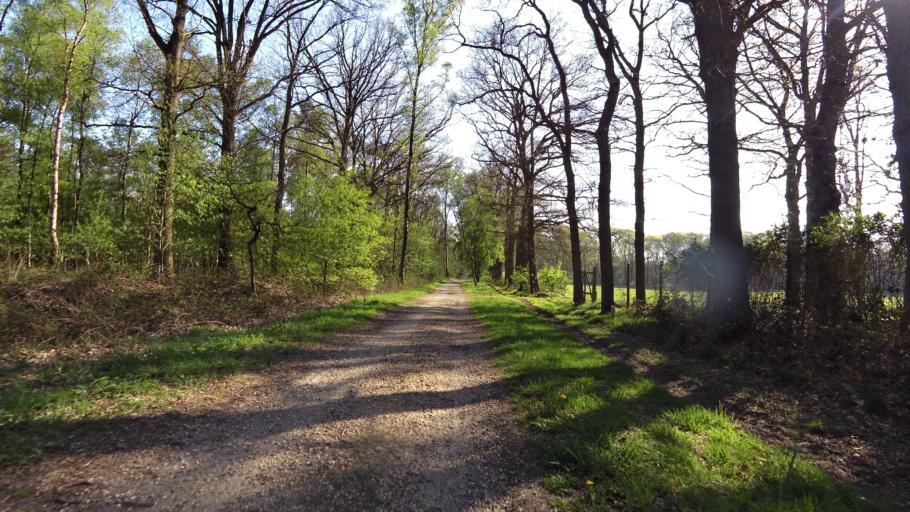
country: NL
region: Gelderland
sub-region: Gemeente Renkum
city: Oosterbeek
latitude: 52.0203
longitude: 5.8355
